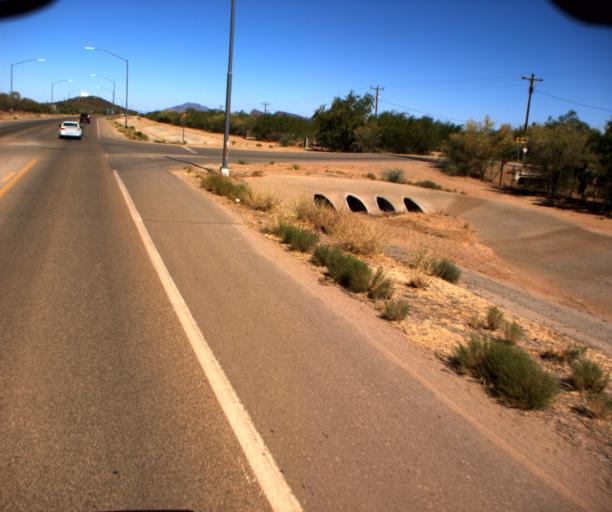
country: US
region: Arizona
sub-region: Pima County
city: Sells
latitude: 31.9175
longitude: -111.8747
